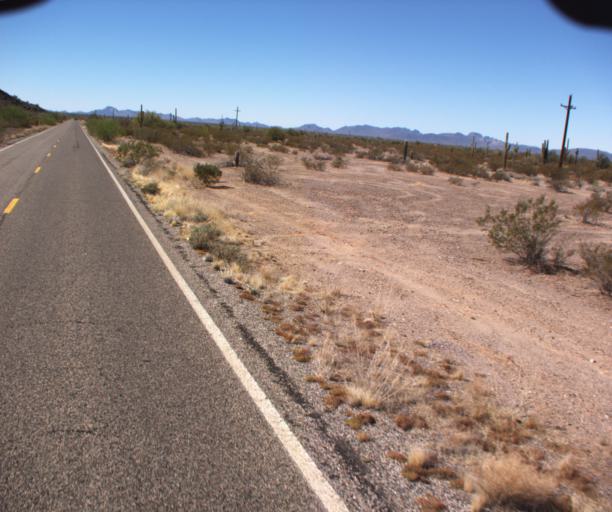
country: US
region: Arizona
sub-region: Pima County
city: Ajo
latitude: 32.2338
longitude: -112.7523
